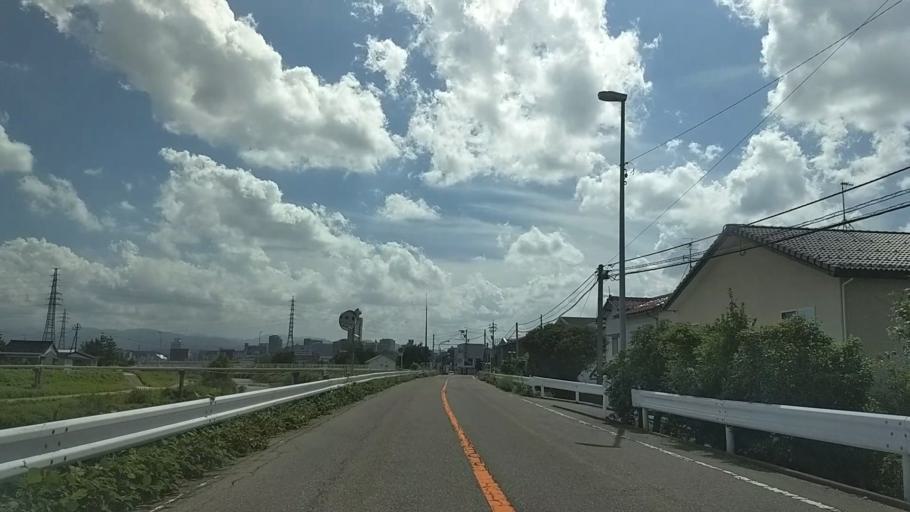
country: JP
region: Ishikawa
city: Kanazawa-shi
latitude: 36.5931
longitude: 136.6497
